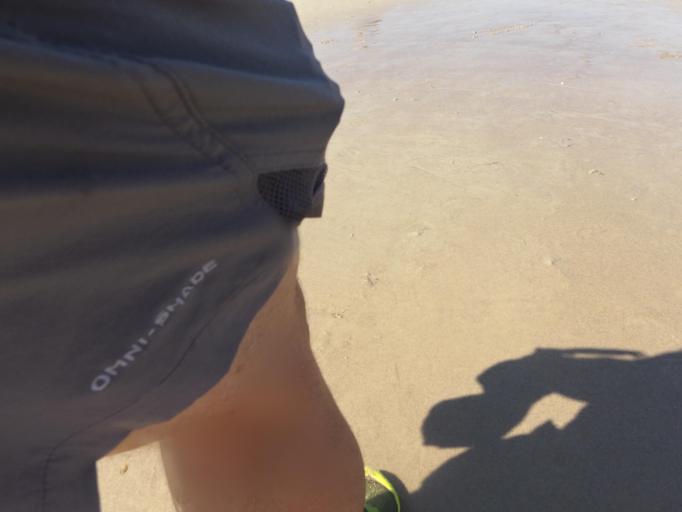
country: US
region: Florida
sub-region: Nassau County
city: Fernandina Beach
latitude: 30.6683
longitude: -81.4297
